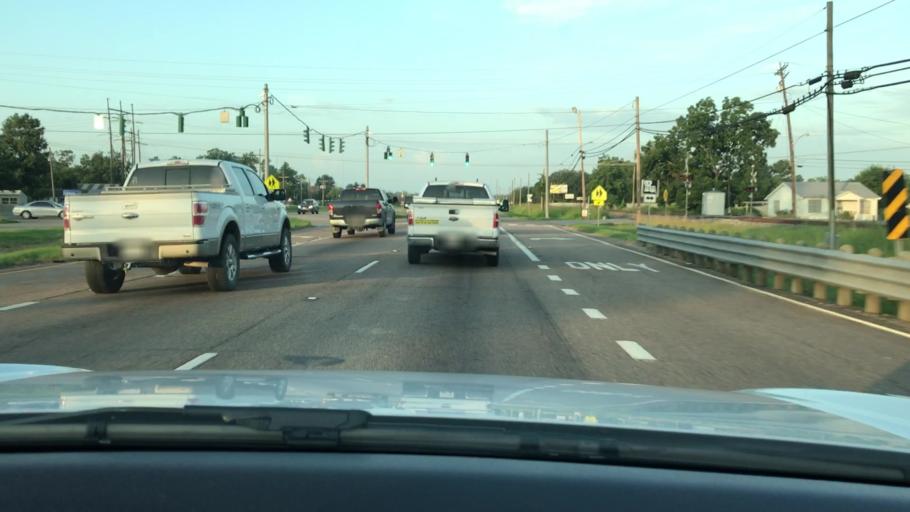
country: US
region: Louisiana
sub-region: West Baton Rouge Parish
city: Brusly
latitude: 30.3817
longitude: -91.2487
